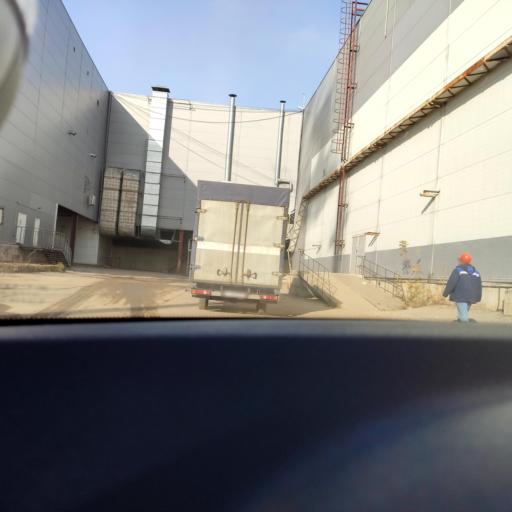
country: RU
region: Samara
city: Petra-Dubrava
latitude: 53.2743
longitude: 50.2725
